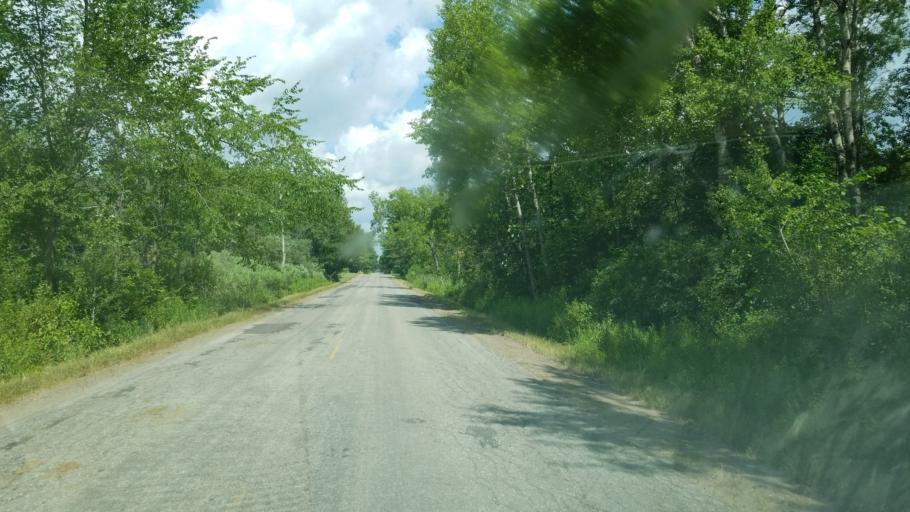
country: US
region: Michigan
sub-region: Mecosta County
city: Canadian Lakes
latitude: 43.5581
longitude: -85.3934
